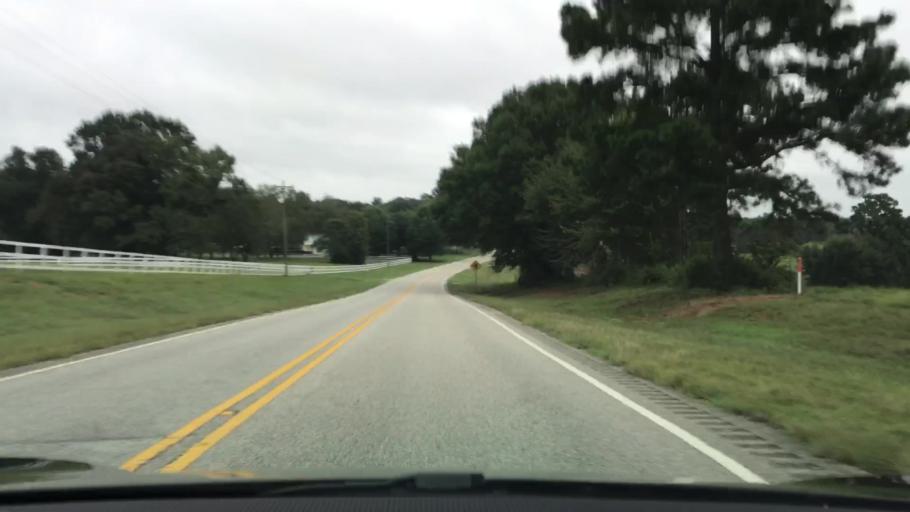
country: US
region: Alabama
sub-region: Coffee County
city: Elba
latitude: 31.3602
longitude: -86.1174
